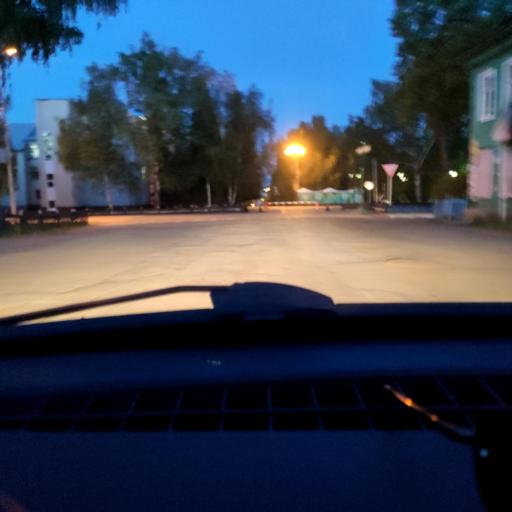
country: RU
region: Bashkortostan
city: Karmaskaly
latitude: 54.3696
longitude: 56.1692
